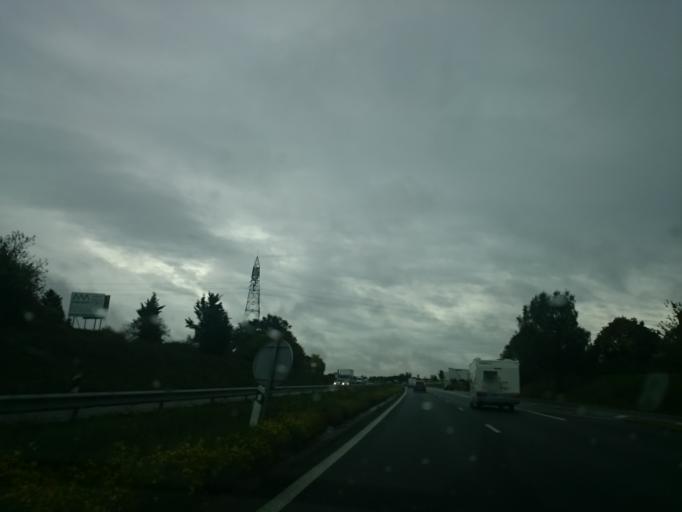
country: FR
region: Pays de la Loire
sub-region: Departement de la Loire-Atlantique
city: Sautron
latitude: 47.2411
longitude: -1.6673
